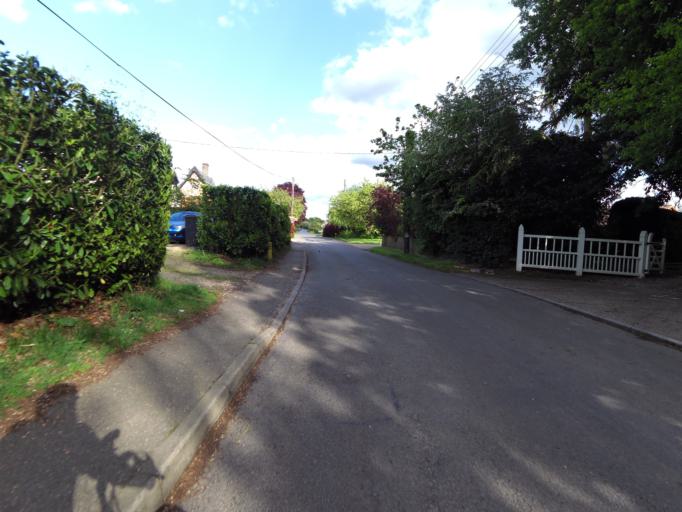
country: GB
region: England
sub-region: Suffolk
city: Stowmarket
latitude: 52.1974
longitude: 0.9566
